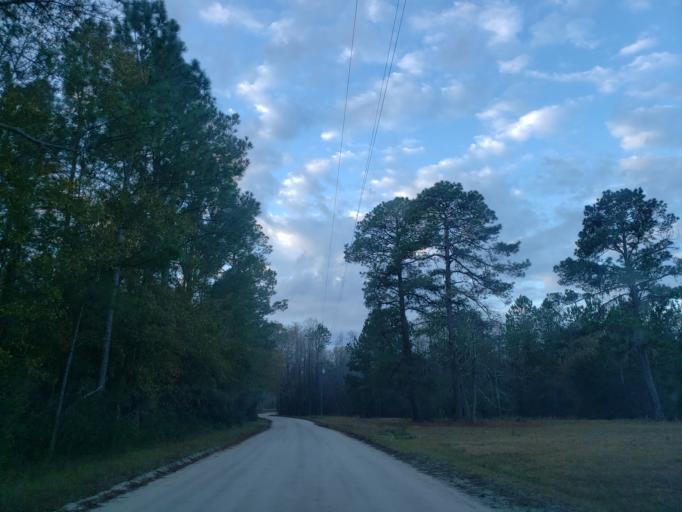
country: US
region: Georgia
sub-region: Chatham County
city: Bloomingdale
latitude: 32.1150
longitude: -81.3442
